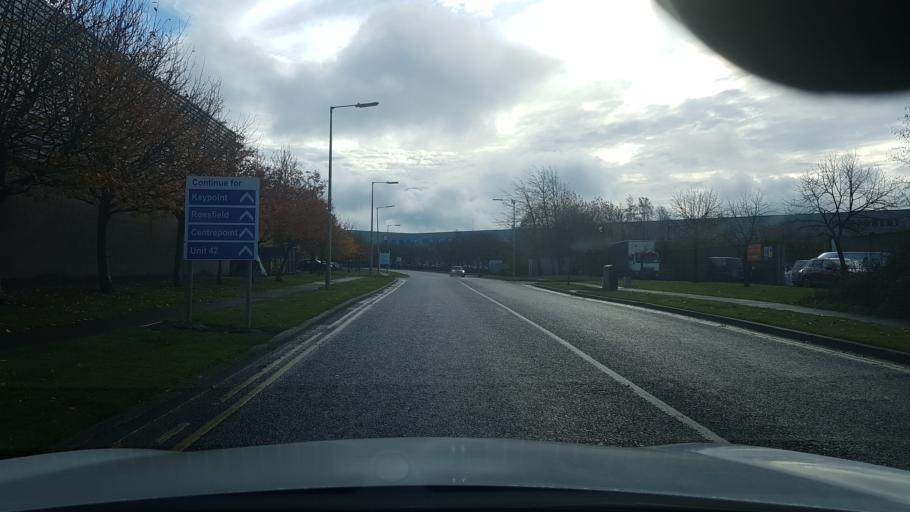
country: IE
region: Leinster
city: Castleknock
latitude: 53.4011
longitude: -6.3481
